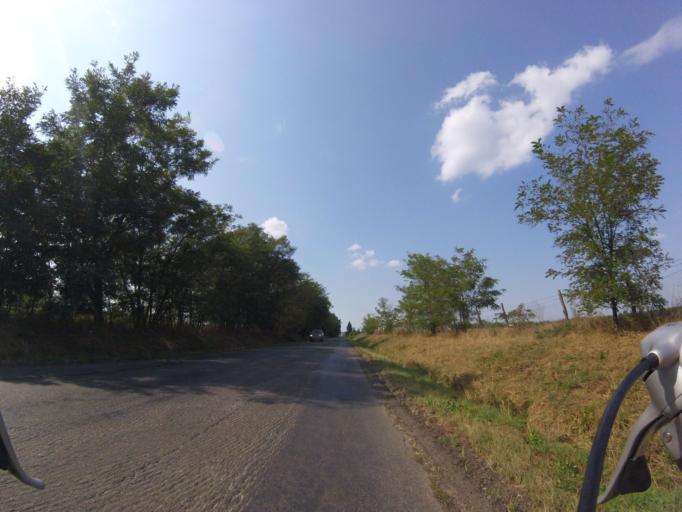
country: HU
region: Szabolcs-Szatmar-Bereg
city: Anarcs
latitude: 48.1702
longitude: 22.1135
